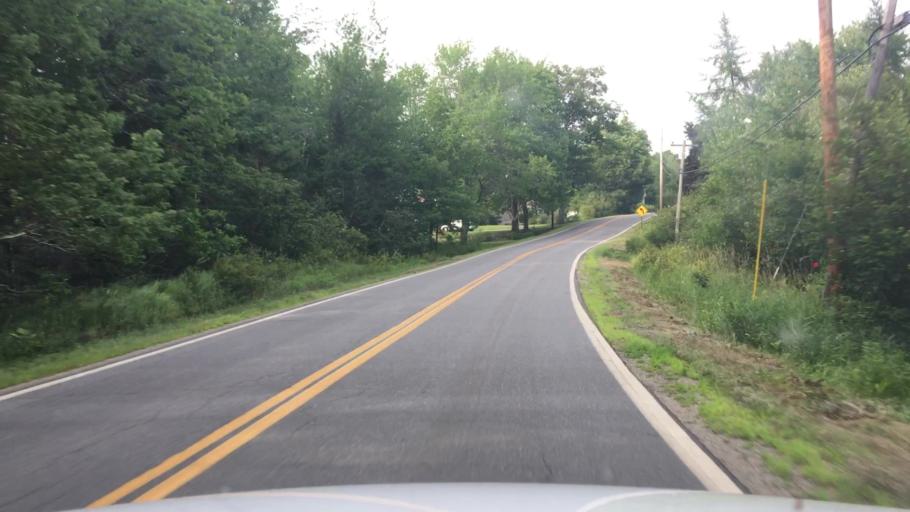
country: US
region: Maine
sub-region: Lincoln County
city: Waldoboro
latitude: 44.1754
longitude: -69.3781
